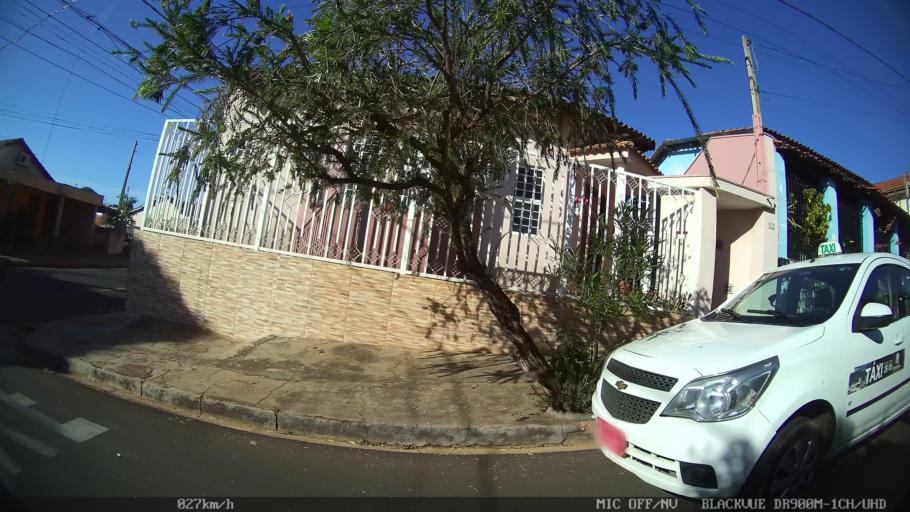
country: BR
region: Sao Paulo
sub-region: Olimpia
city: Olimpia
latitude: -20.7361
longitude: -48.9057
